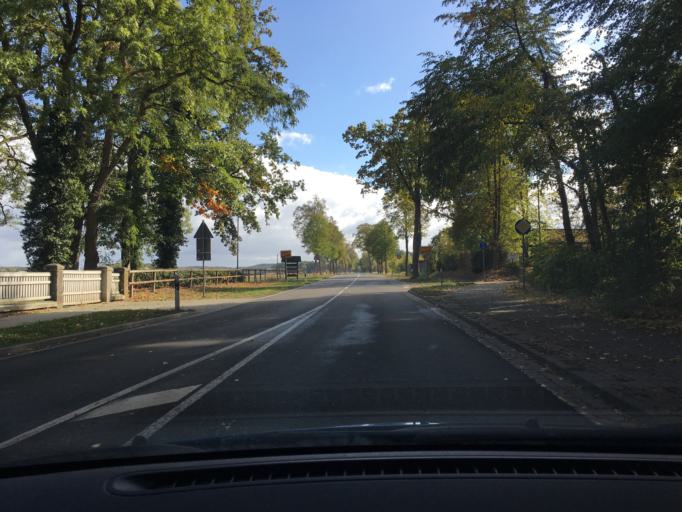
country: DE
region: Lower Saxony
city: Bergen an der Dumme
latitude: 52.8893
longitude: 10.9690
